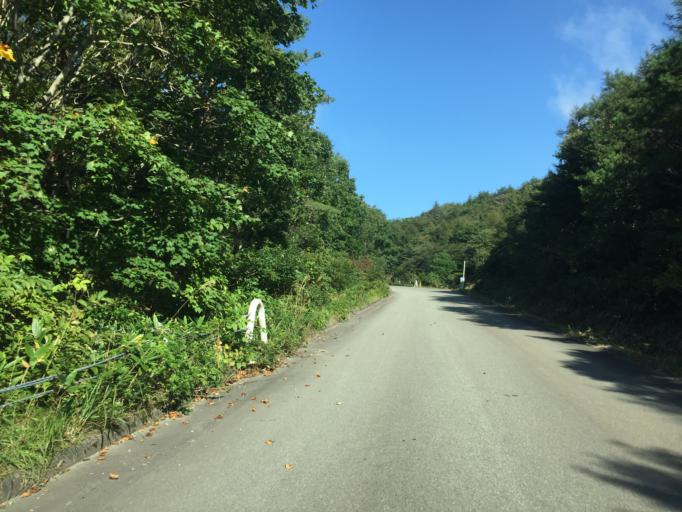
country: JP
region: Fukushima
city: Inawashiro
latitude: 37.4645
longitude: 139.9933
